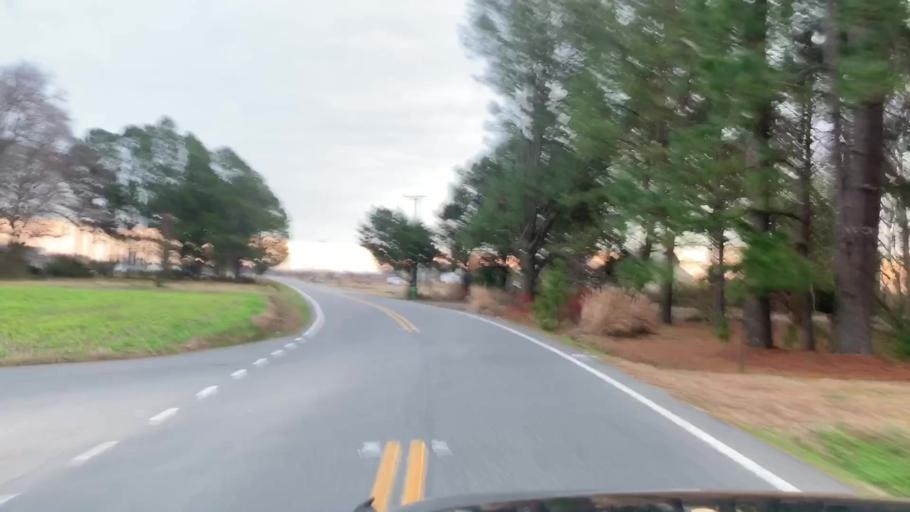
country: US
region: North Carolina
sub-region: Currituck County
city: Moyock
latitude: 36.6241
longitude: -76.1593
